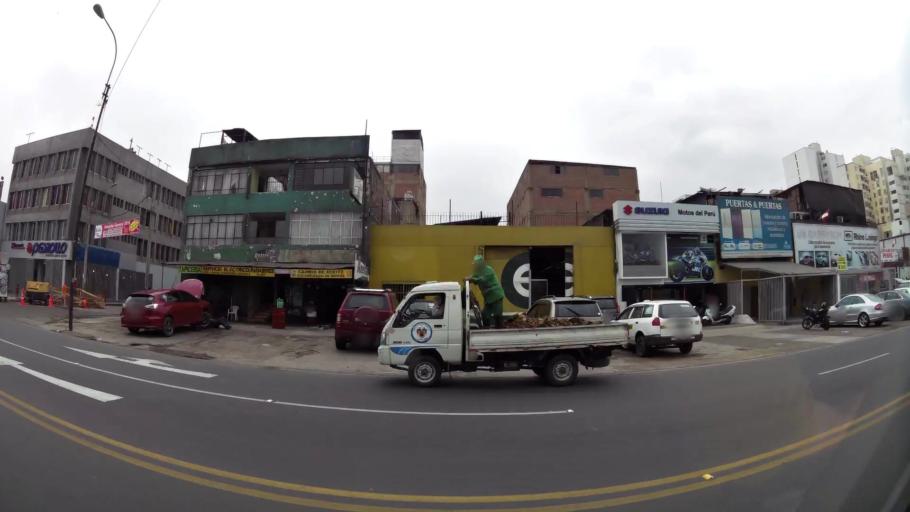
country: PE
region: Lima
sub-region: Lima
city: Surco
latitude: -12.1173
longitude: -77.0184
